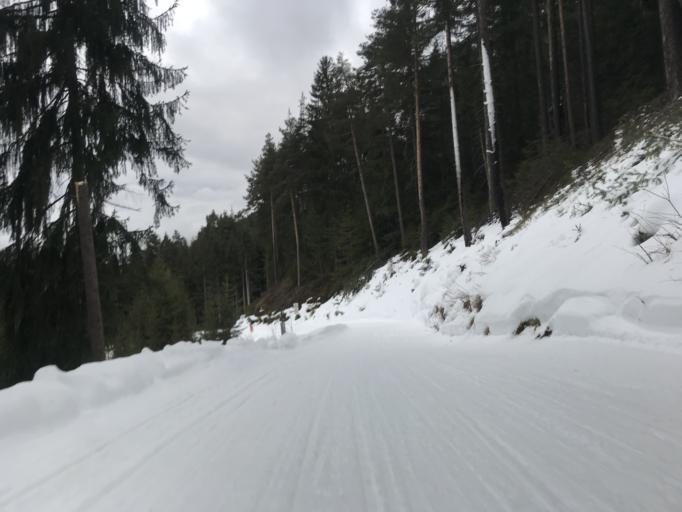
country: IT
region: Trentino-Alto Adige
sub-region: Bolzano
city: Bressanone
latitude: 46.6920
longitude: 11.6882
